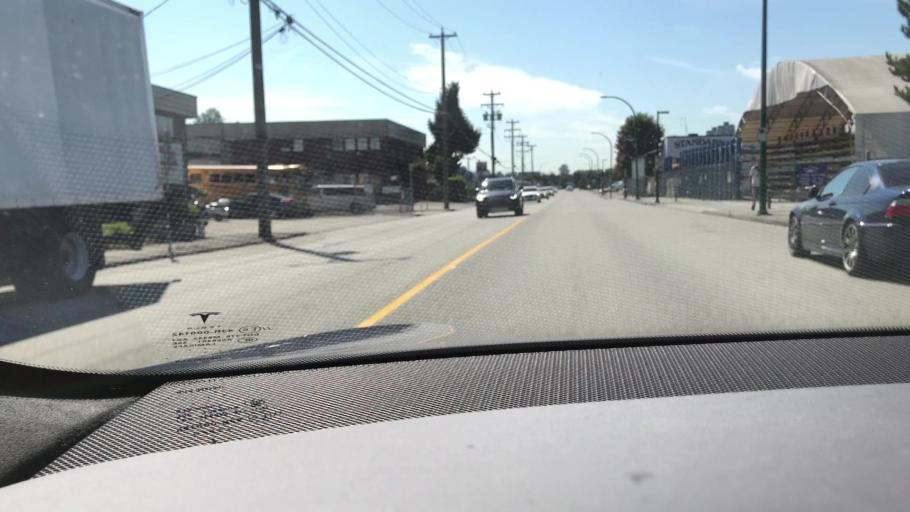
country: CA
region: British Columbia
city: Burnaby
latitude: 49.2608
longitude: -122.9904
